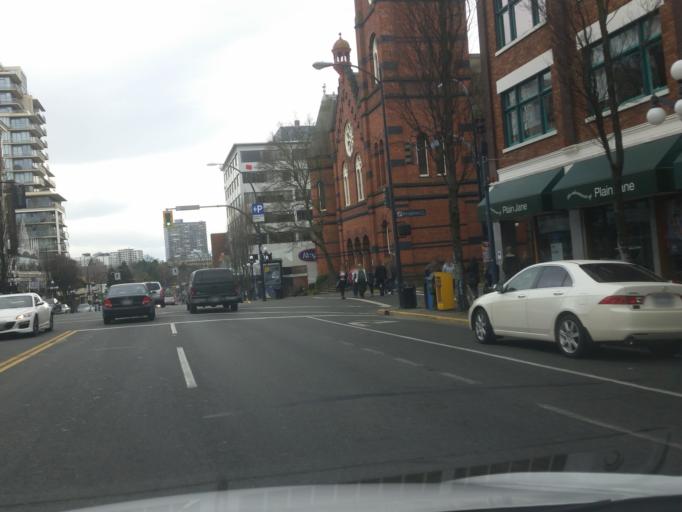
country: CA
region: British Columbia
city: Victoria
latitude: 48.4242
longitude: -123.3656
